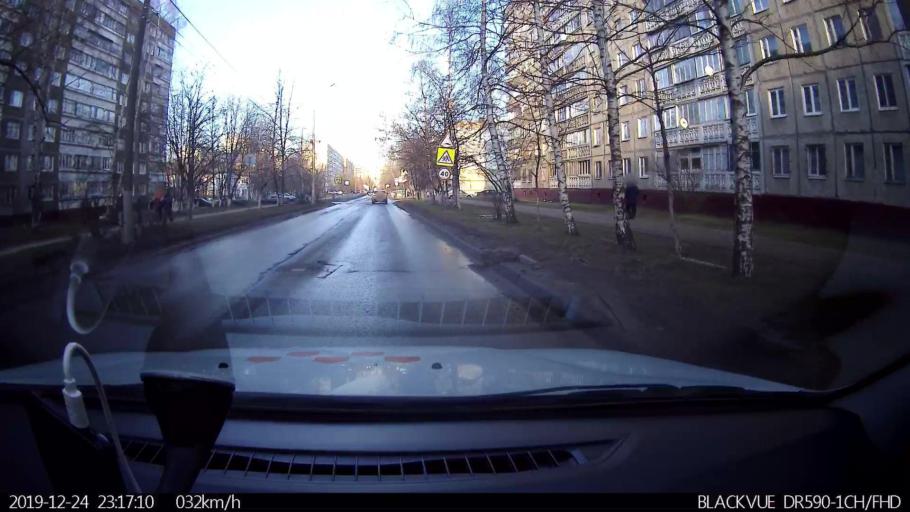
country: RU
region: Nizjnij Novgorod
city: Gorbatovka
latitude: 56.2537
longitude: 43.8585
